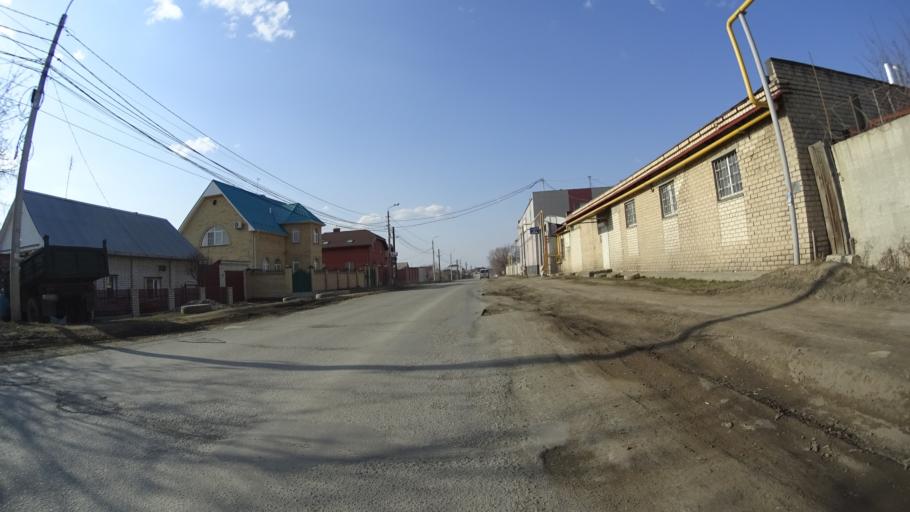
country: RU
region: Chelyabinsk
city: Novosineglazovskiy
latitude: 55.1084
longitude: 61.3345
